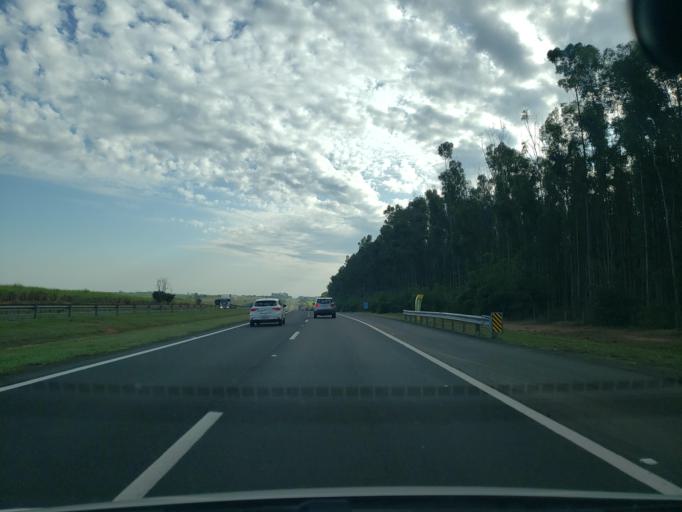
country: BR
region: Sao Paulo
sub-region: Guararapes
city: Guararapes
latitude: -21.1994
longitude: -50.5679
